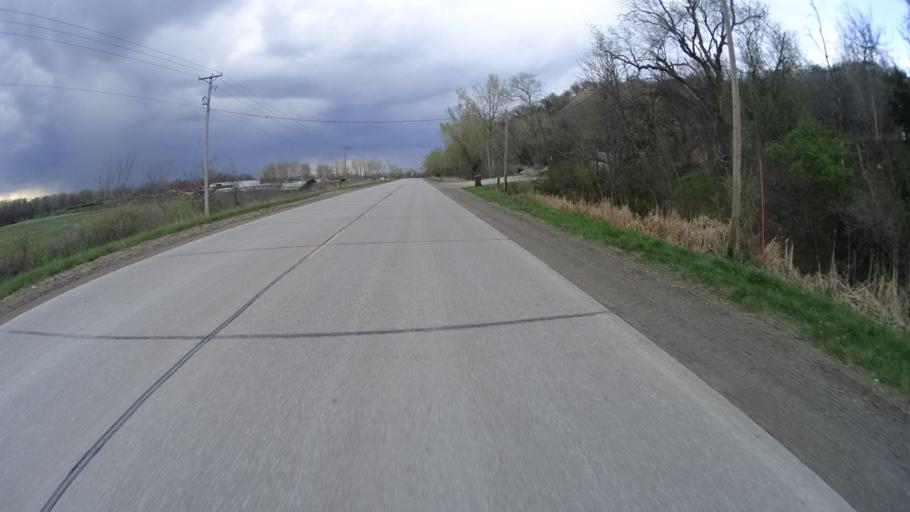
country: US
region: Iowa
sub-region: Mills County
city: Glenwood
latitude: 41.0769
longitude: -95.8134
